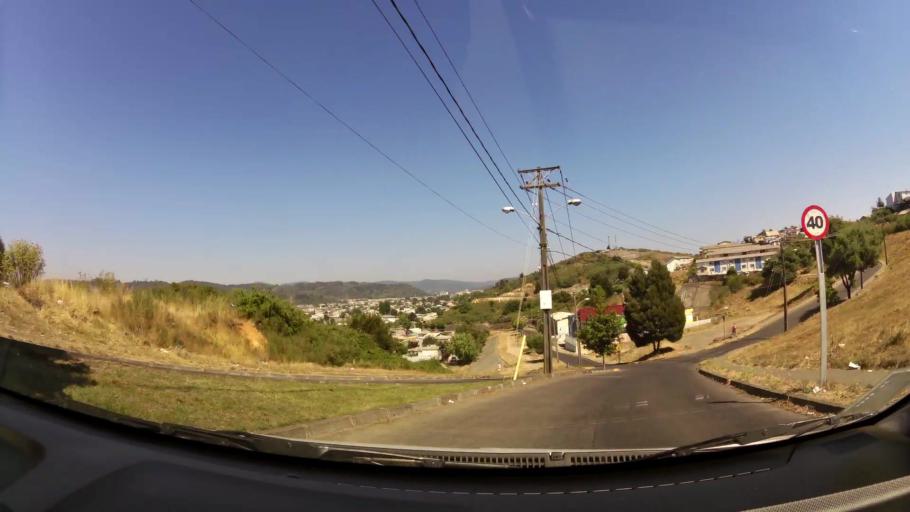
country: CL
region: Biobio
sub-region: Provincia de Concepcion
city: Concepcion
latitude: -36.7901
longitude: -73.0420
